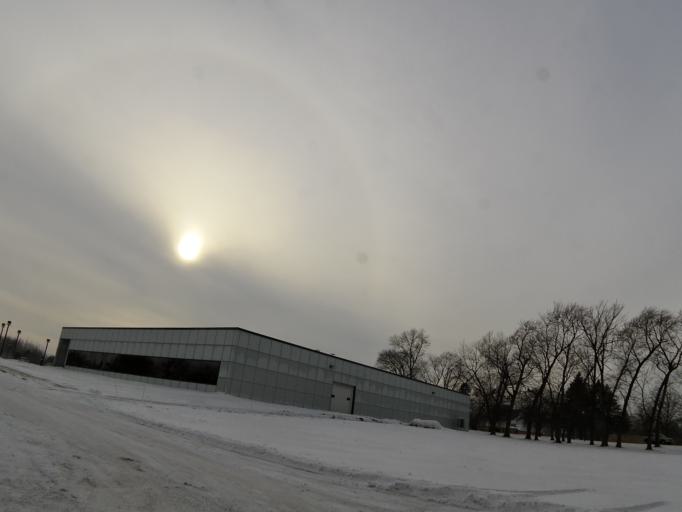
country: US
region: Minnesota
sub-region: McLeod County
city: Hutchinson
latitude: 44.9024
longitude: -94.3542
